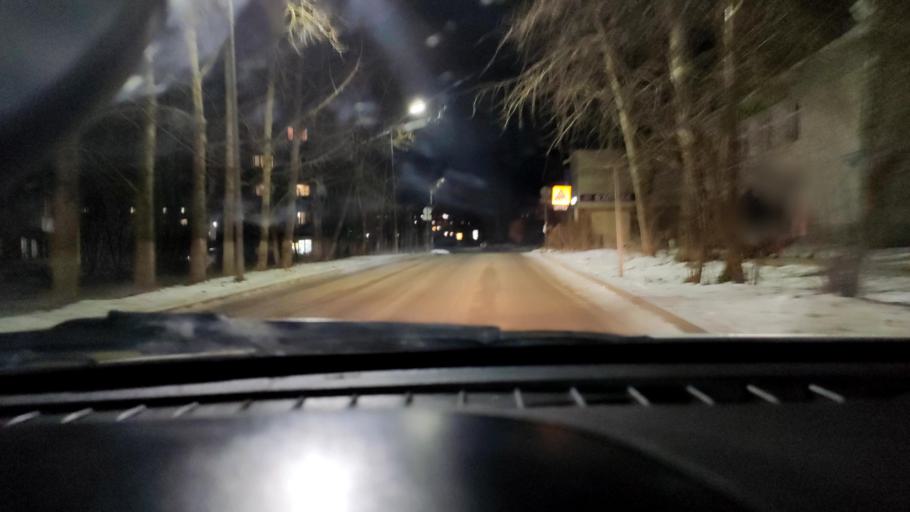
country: RU
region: Perm
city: Lobanovo
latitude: 57.8622
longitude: 56.2888
